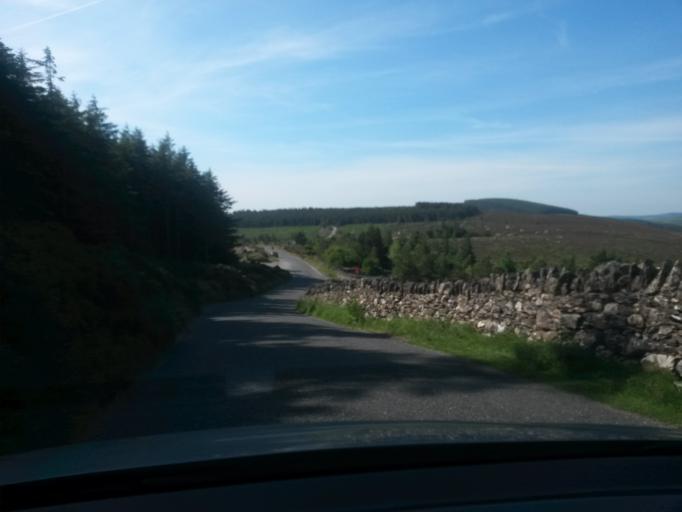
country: IE
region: Leinster
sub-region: Wicklow
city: Enniskerry
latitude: 53.0971
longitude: -6.2512
